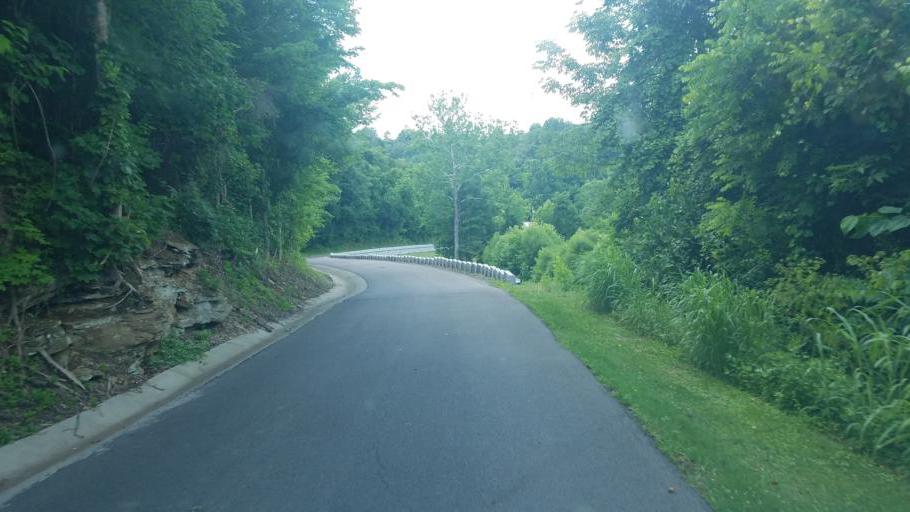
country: US
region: Ohio
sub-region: Gallia County
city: Gallipolis
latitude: 38.7989
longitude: -82.2230
